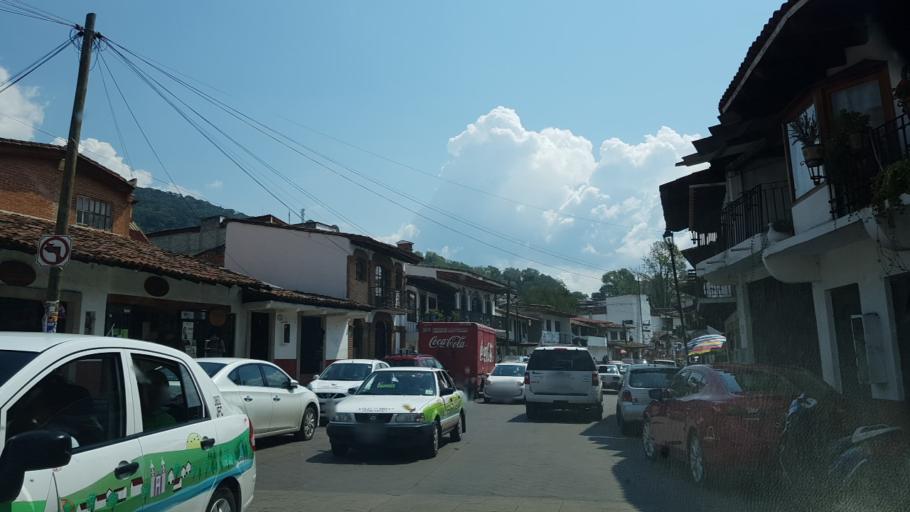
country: MX
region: Mexico
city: Valle de Bravo
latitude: 19.1993
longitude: -100.1320
